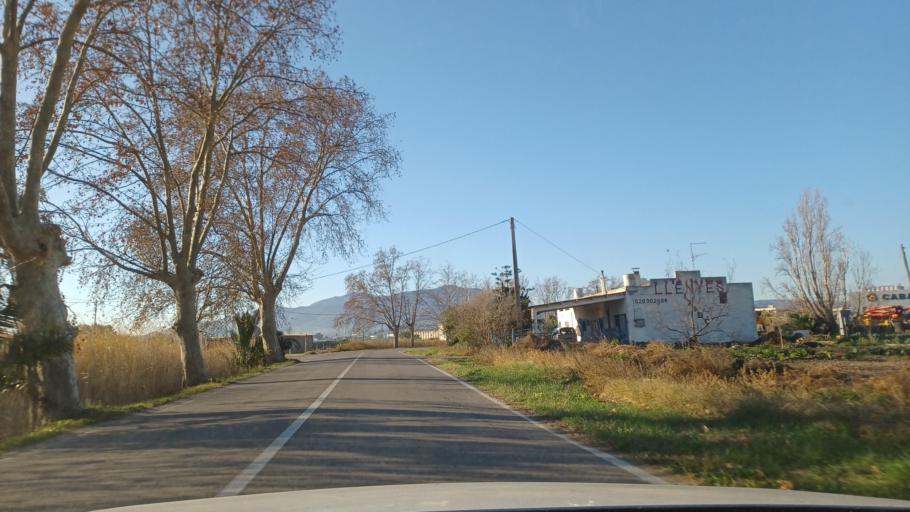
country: ES
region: Catalonia
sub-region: Provincia de Tarragona
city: Amposta
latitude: 40.7047
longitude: 0.5898
